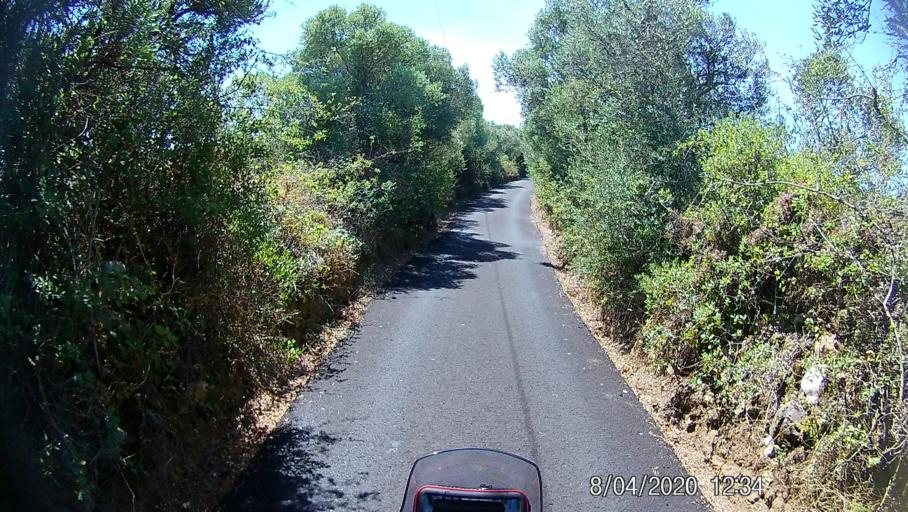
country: PT
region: Lisbon
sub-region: Sintra
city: Rio de Mouro
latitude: 38.7522
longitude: -9.3609
